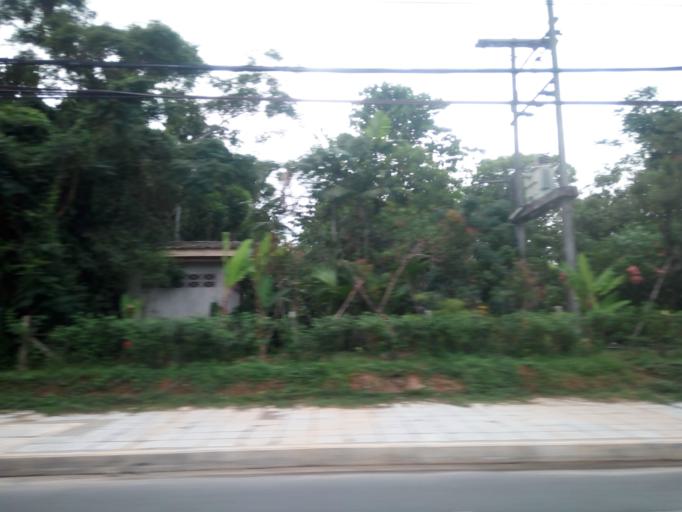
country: TH
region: Phuket
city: Thalang
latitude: 8.0182
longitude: 98.3372
